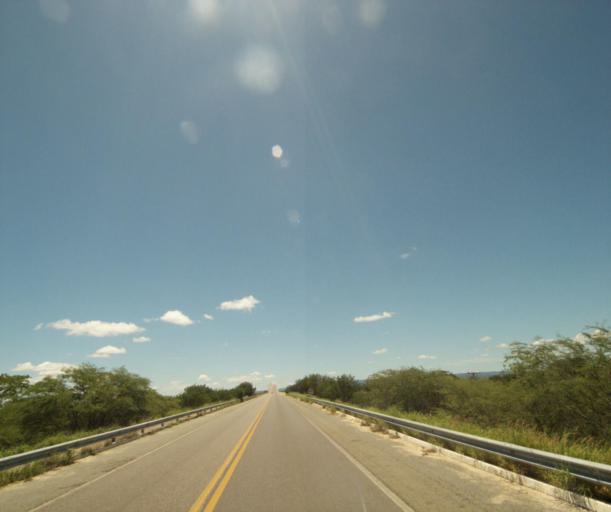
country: BR
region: Bahia
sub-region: Carinhanha
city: Carinhanha
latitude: -14.3216
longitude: -43.7760
